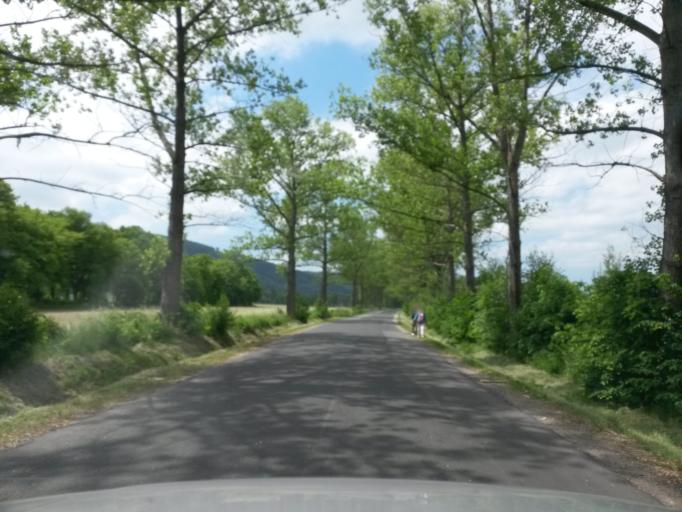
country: PL
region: Lower Silesian Voivodeship
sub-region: Powiat jeleniogorski
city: Piechowice
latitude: 50.8514
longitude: 15.6351
